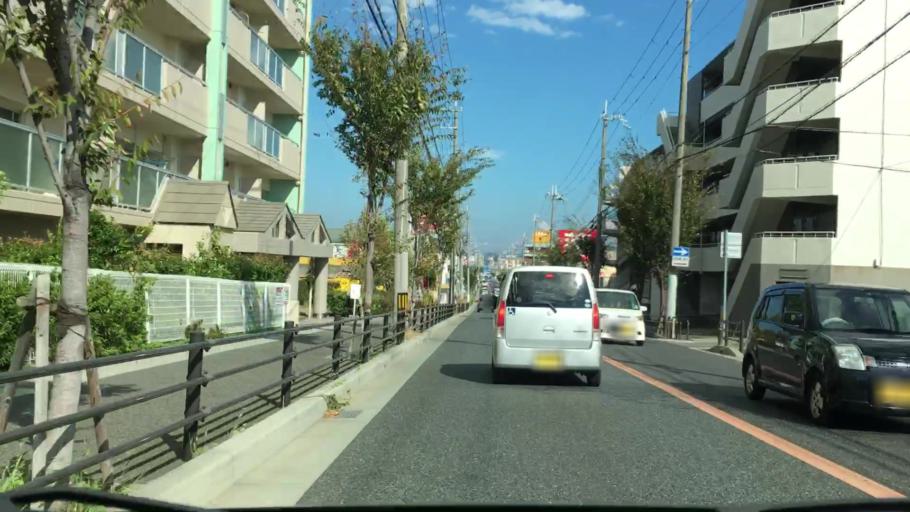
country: JP
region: Hyogo
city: Akashi
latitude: 34.6693
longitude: 134.9743
